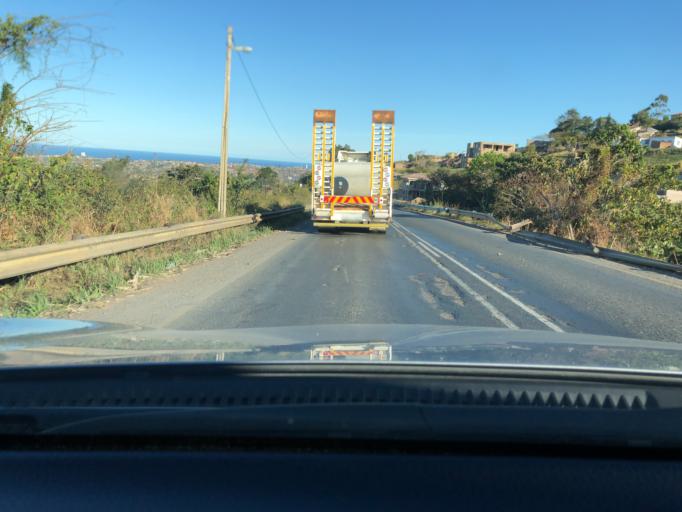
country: ZA
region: KwaZulu-Natal
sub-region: eThekwini Metropolitan Municipality
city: Umkomaas
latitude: -30.0186
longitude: 30.8090
